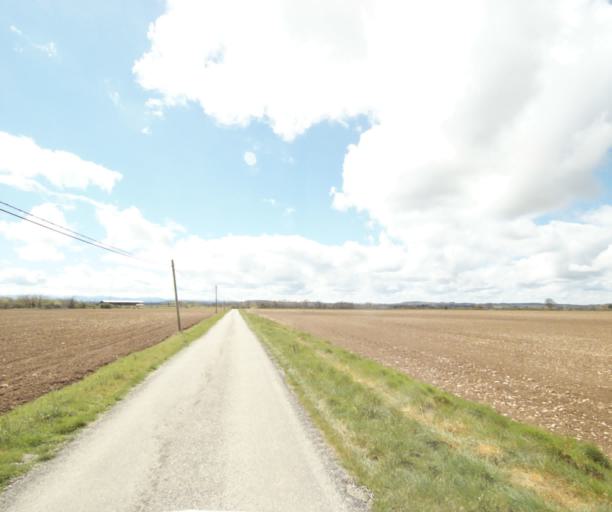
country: FR
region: Midi-Pyrenees
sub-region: Departement de l'Ariege
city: Saverdun
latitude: 43.2495
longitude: 1.6060
